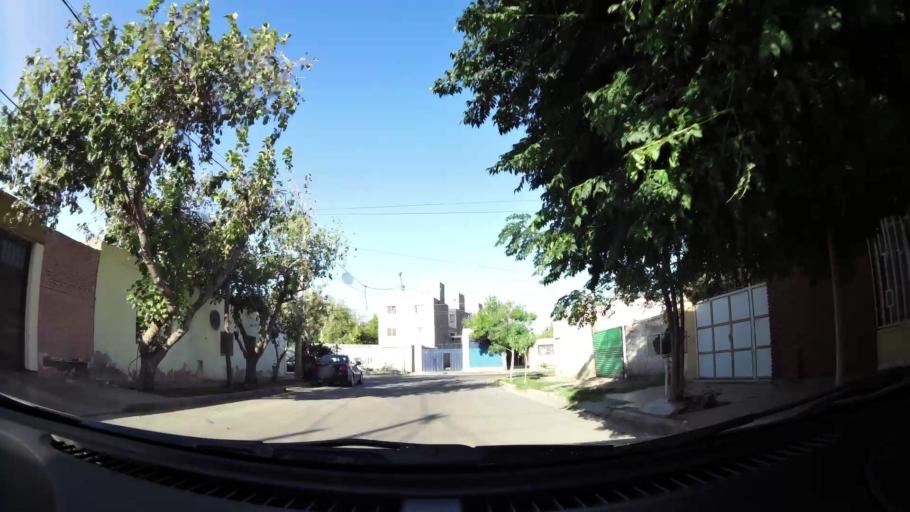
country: AR
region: San Juan
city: San Juan
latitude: -31.5485
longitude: -68.5186
